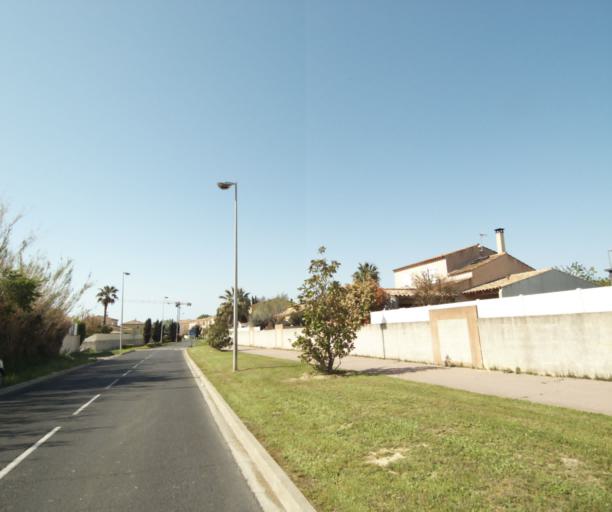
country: FR
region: Languedoc-Roussillon
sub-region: Departement de l'Herault
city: Lattes
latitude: 43.5764
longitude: 3.9070
